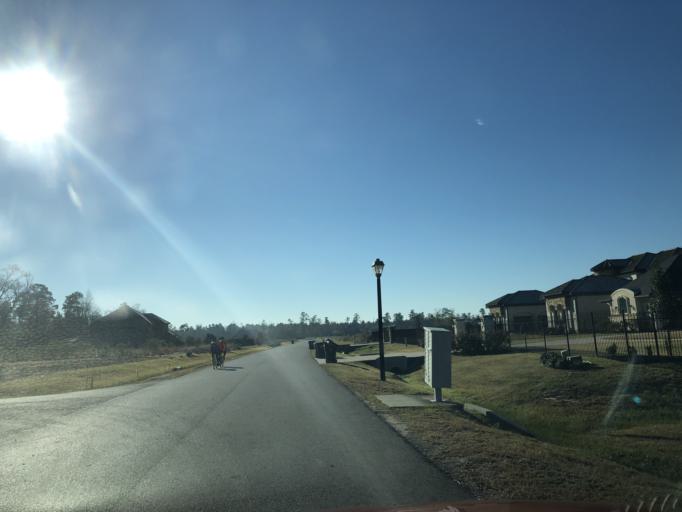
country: US
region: Texas
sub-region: Montgomery County
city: Porter Heights
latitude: 30.0769
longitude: -95.3196
